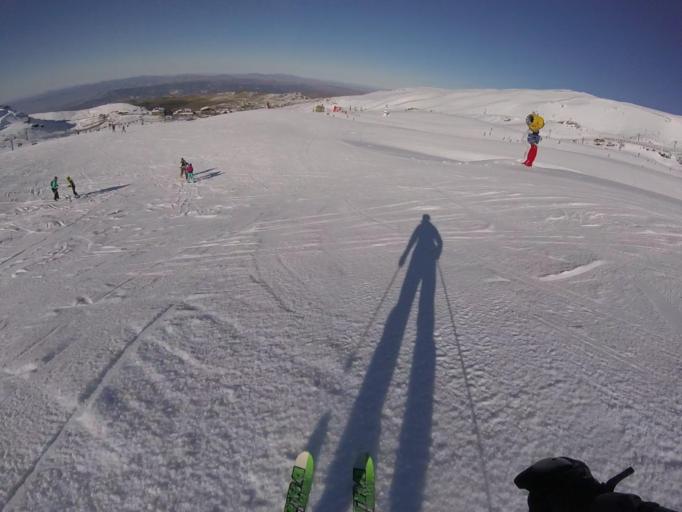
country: ES
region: Andalusia
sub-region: Provincia de Granada
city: Guejar-Sierra
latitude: 37.0658
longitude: -3.3863
